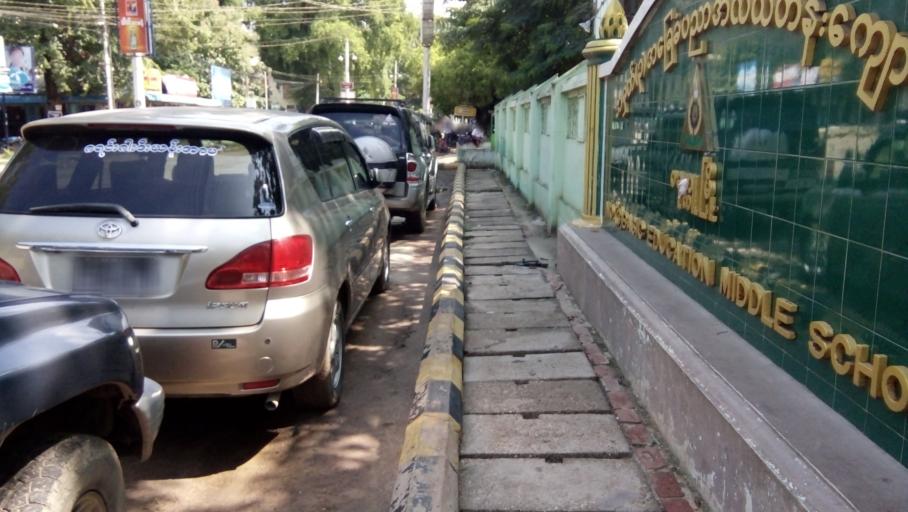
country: MM
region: Magway
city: Pakokku
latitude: 21.3347
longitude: 95.0904
